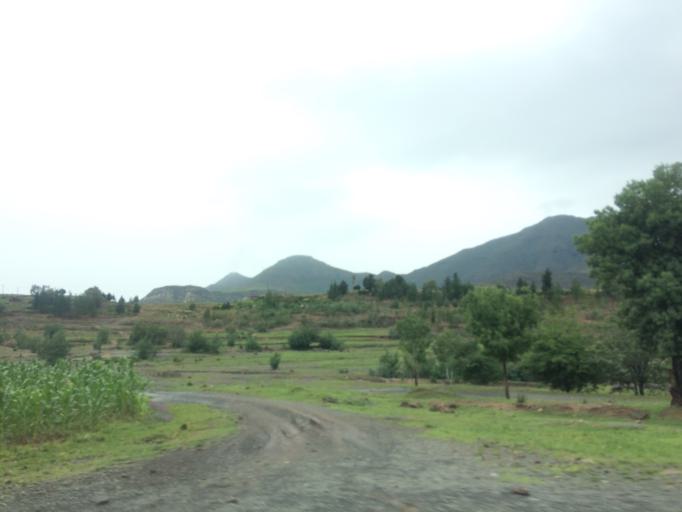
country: LS
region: Mafeteng
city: Mafeteng
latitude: -29.7820
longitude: 27.5218
